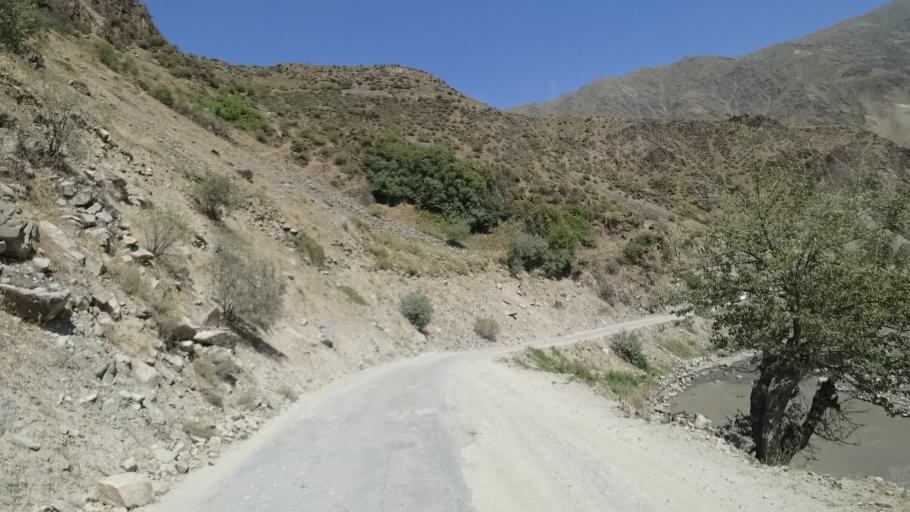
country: AF
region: Badakhshan
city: Maymay
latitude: 38.4438
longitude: 70.9434
